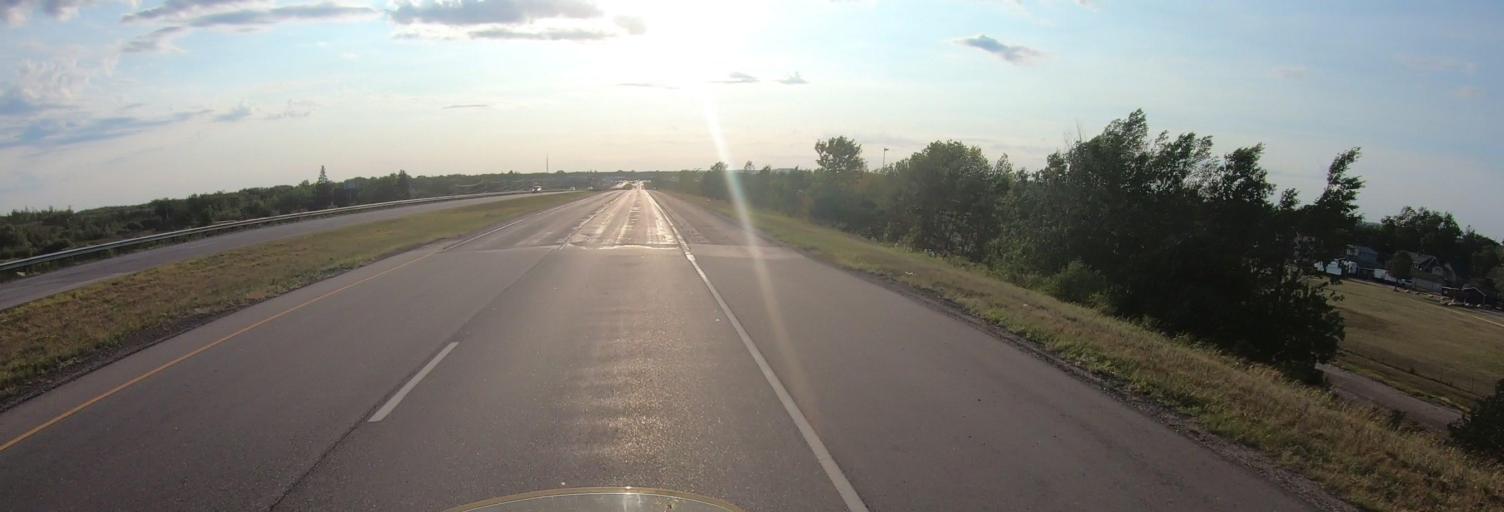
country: US
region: Minnesota
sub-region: Saint Louis County
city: Virginia
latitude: 47.5101
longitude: -92.5370
